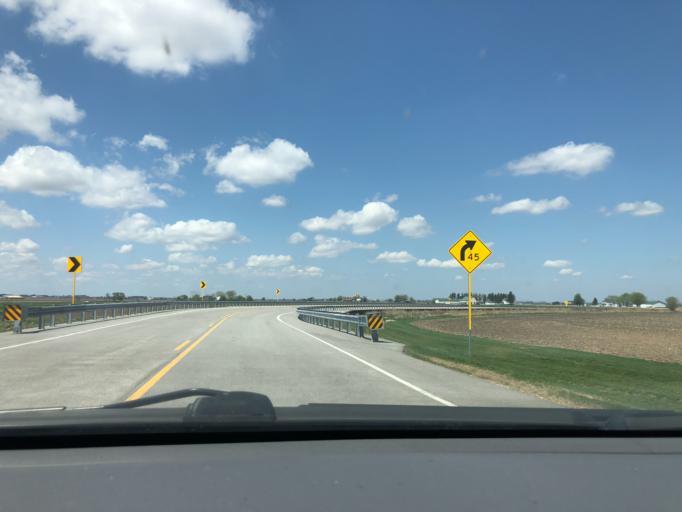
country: US
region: Illinois
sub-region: Kane County
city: Hampshire
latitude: 42.1065
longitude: -88.5533
